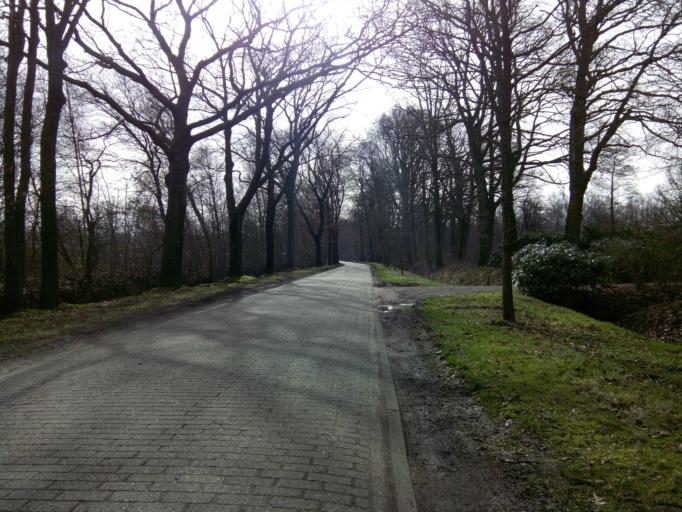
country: NL
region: Utrecht
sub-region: Gemeente Utrechtse Heuvelrug
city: Maarn
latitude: 52.0745
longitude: 5.3851
